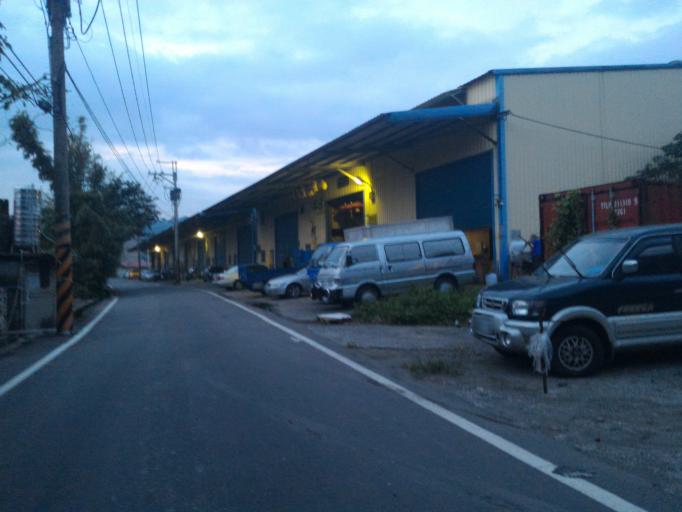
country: TW
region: Taiwan
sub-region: Taoyuan
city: Taoyuan
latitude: 24.9581
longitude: 121.3946
